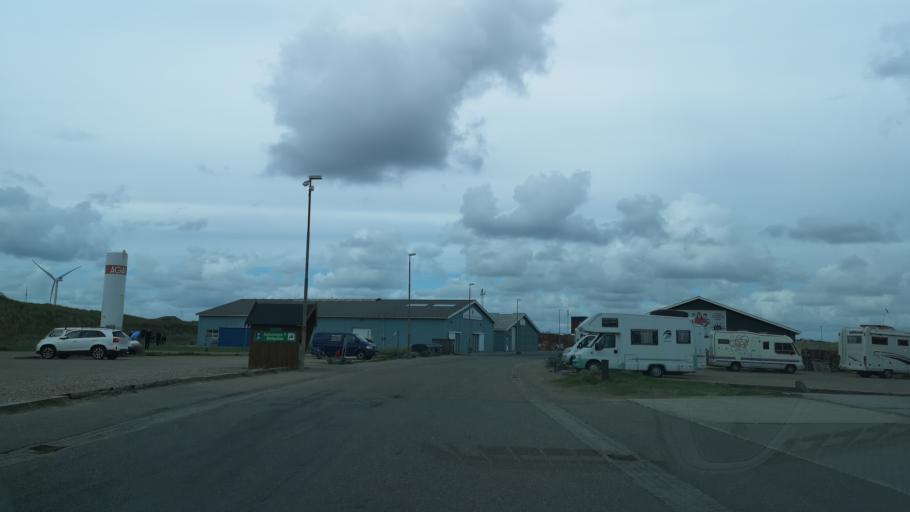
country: DK
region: Central Jutland
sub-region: Ringkobing-Skjern Kommune
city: Hvide Sande
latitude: 55.9974
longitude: 8.1222
